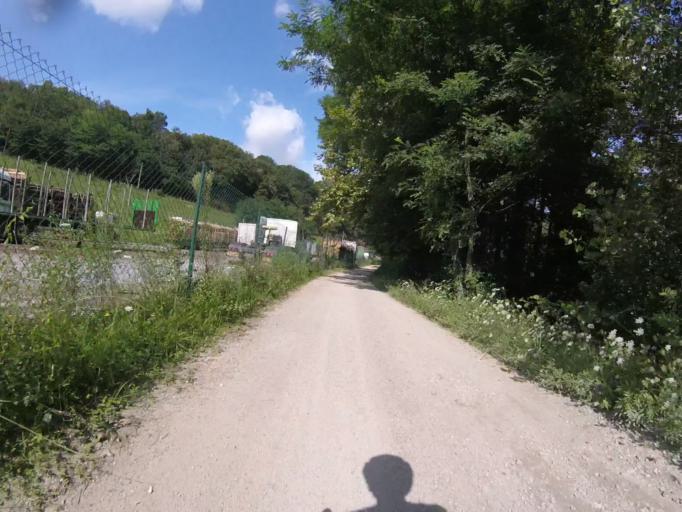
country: ES
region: Navarre
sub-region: Provincia de Navarra
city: Igantzi
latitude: 43.2260
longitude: -1.6770
